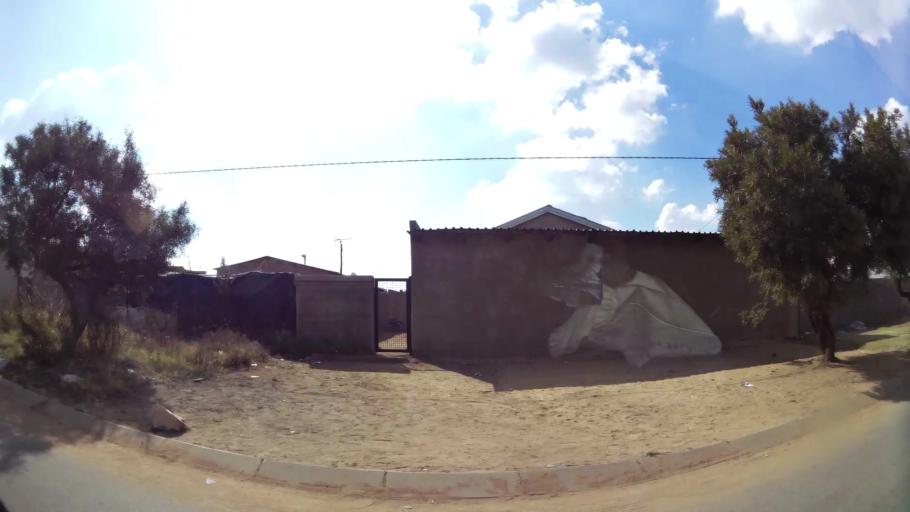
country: ZA
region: Gauteng
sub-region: City of Johannesburg Metropolitan Municipality
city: Roodepoort
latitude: -26.1910
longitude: 27.8739
